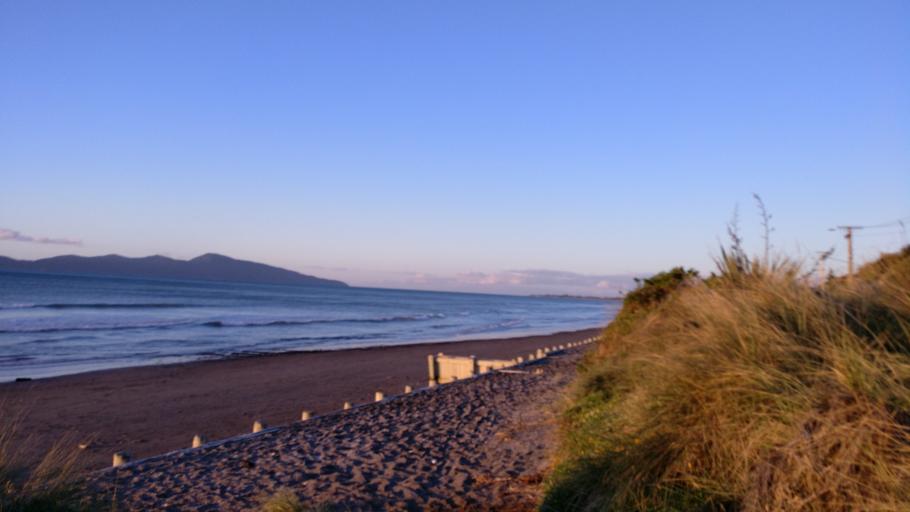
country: NZ
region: Wellington
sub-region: Kapiti Coast District
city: Paraparaumu
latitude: -40.9783
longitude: 174.9563
